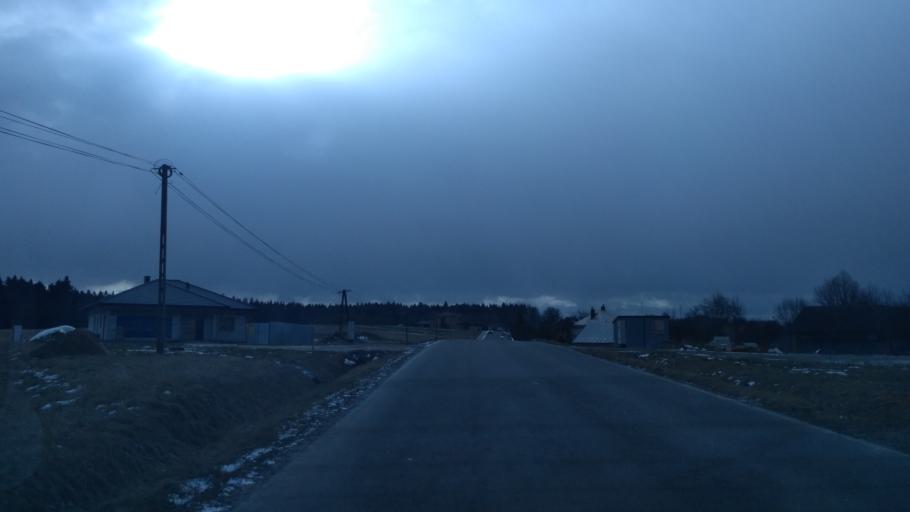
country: PL
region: Subcarpathian Voivodeship
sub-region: Powiat rzeszowski
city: Blazowa
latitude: 49.8439
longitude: 22.0889
